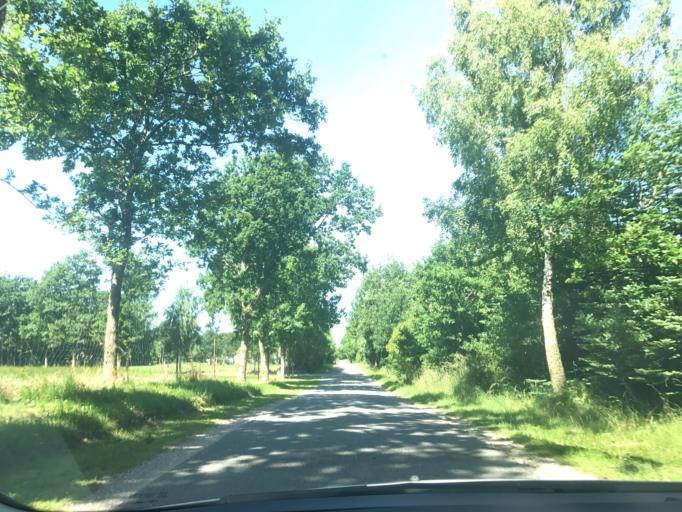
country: DK
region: Central Jutland
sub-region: Syddjurs Kommune
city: Ryomgard
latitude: 56.4219
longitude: 10.5191
